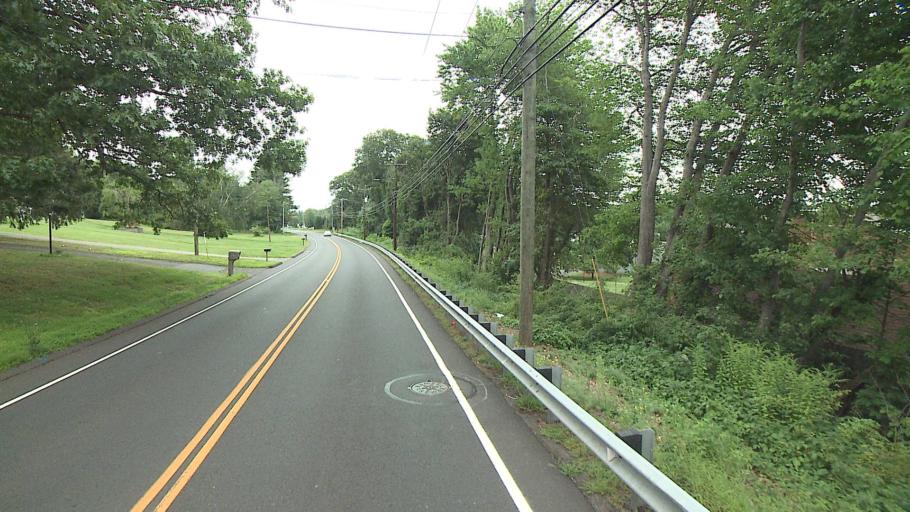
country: US
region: Connecticut
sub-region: Middlesex County
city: Cromwell
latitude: 41.6215
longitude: -72.6752
